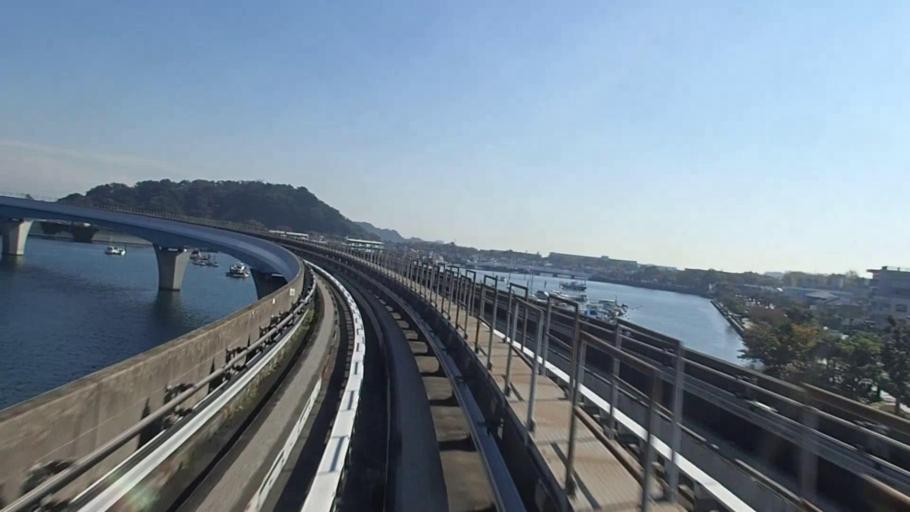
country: JP
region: Kanagawa
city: Zushi
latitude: 35.3285
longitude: 139.6259
